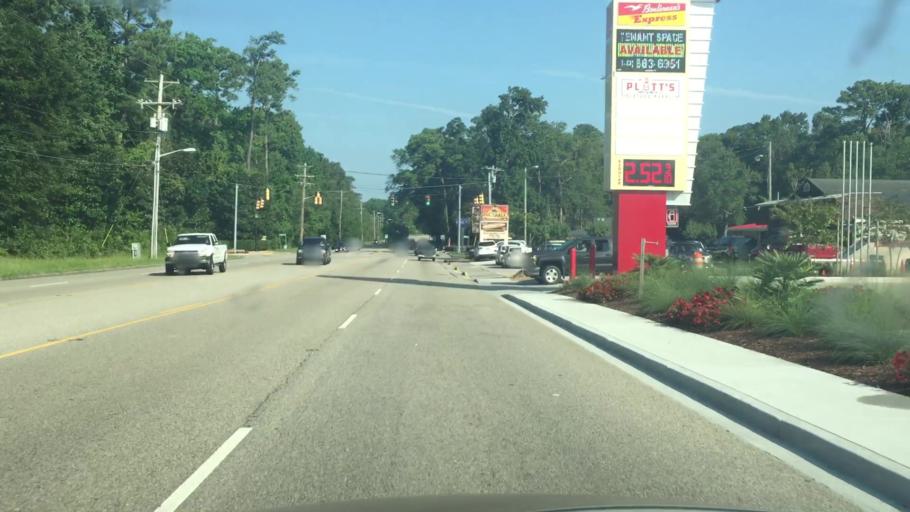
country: US
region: South Carolina
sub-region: Horry County
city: North Myrtle Beach
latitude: 33.8418
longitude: -78.6472
